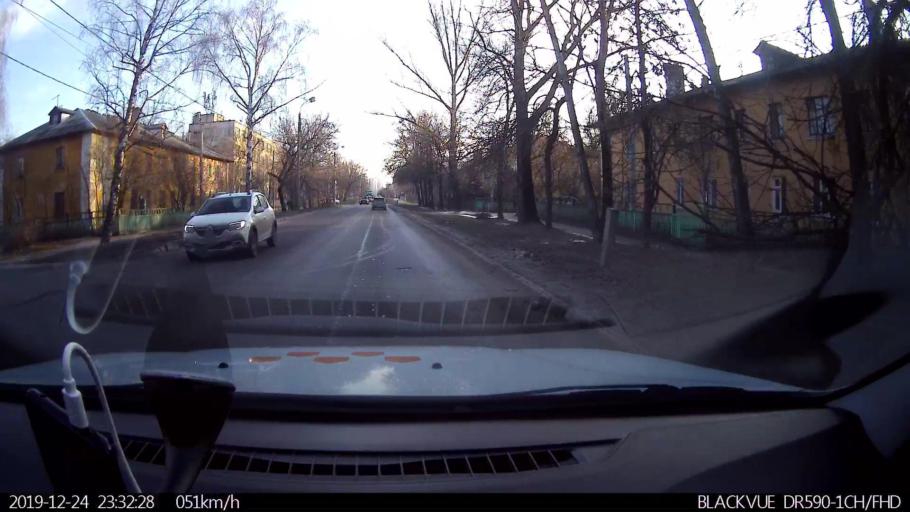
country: RU
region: Nizjnij Novgorod
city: Burevestnik
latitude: 56.2284
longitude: 43.8508
